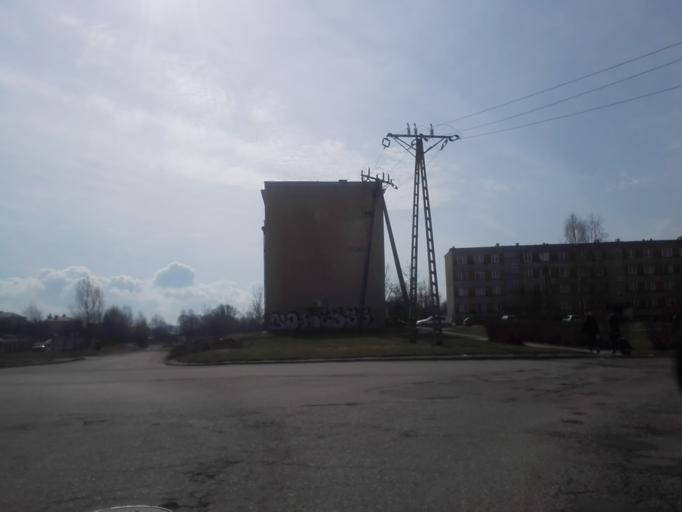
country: PL
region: Podlasie
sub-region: Powiat sejnenski
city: Sejny
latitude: 54.1059
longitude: 23.3415
